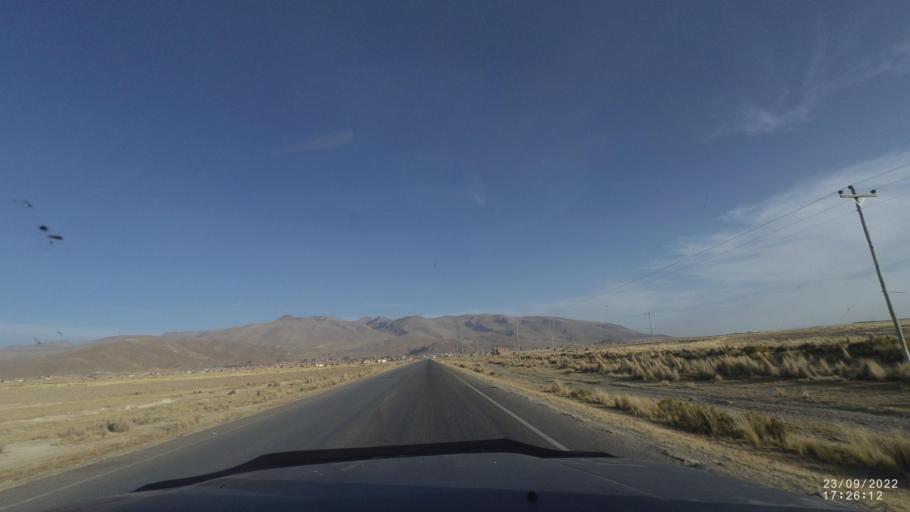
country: BO
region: Oruro
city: Challapata
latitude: -18.8816
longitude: -66.7884
